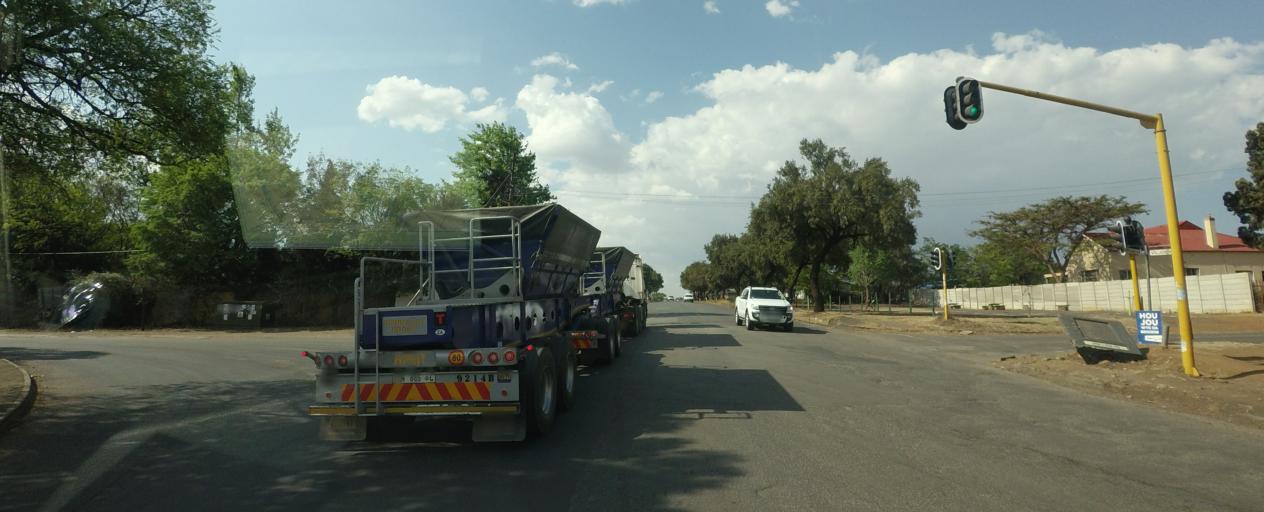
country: ZA
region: Mpumalanga
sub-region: Ehlanzeni District
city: Lydenburg
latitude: -25.0984
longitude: 30.4543
